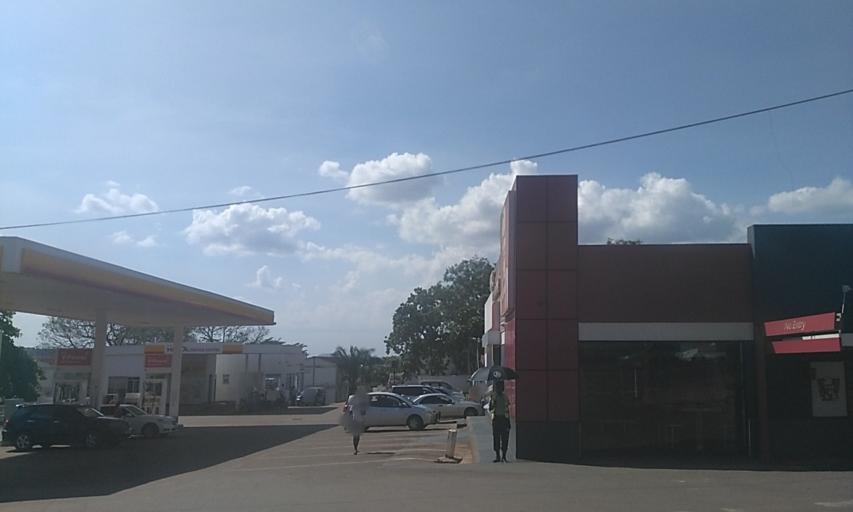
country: UG
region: Central Region
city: Kampala Central Division
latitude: 0.3449
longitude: 32.5966
